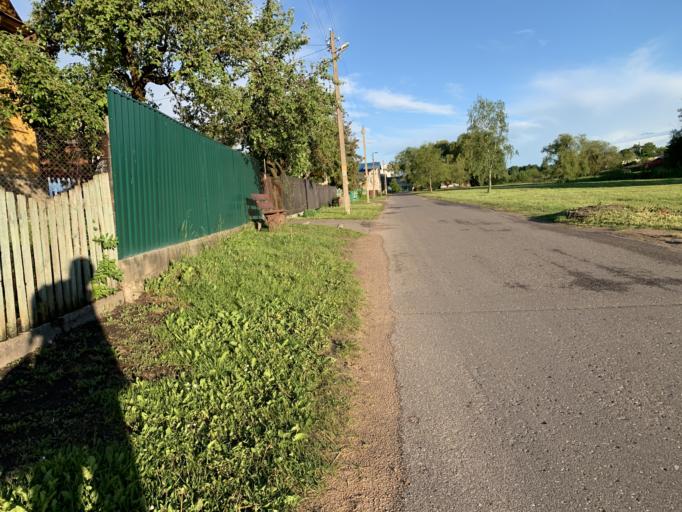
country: BY
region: Minsk
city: Nyasvizh
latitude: 53.2126
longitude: 26.6916
